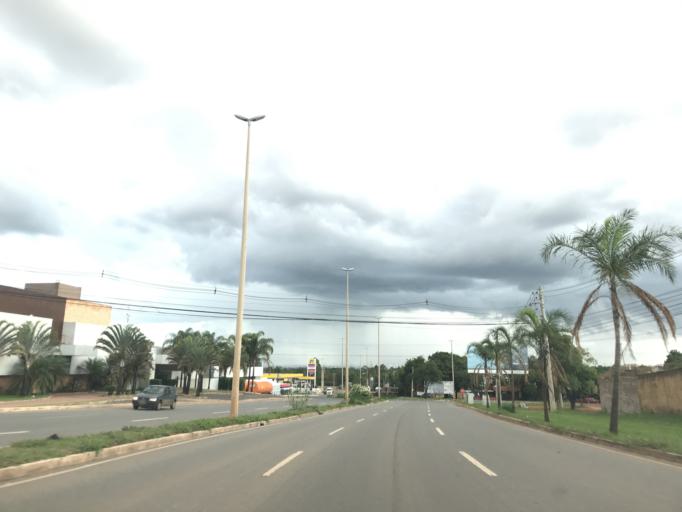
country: BR
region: Federal District
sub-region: Brasilia
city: Brasilia
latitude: -15.7998
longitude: -47.9713
